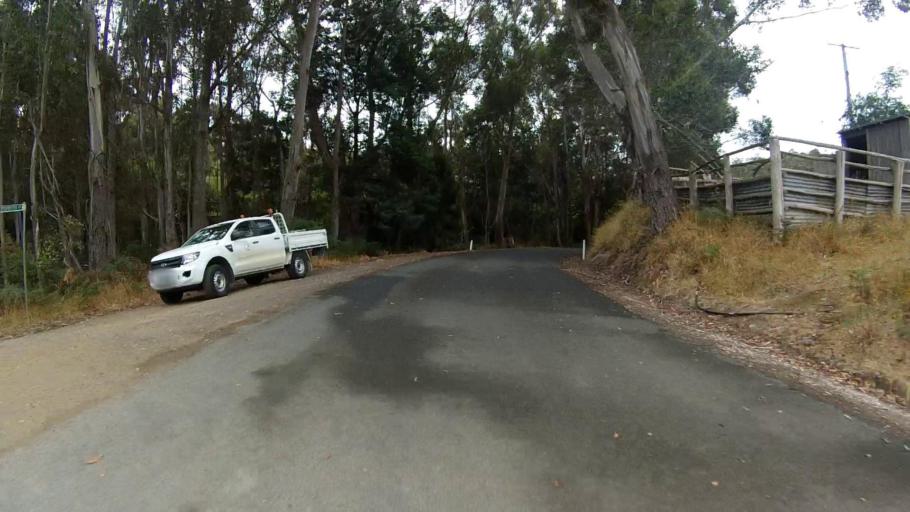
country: AU
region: Tasmania
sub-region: Huon Valley
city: Cygnet
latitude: -43.2349
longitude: 147.1568
